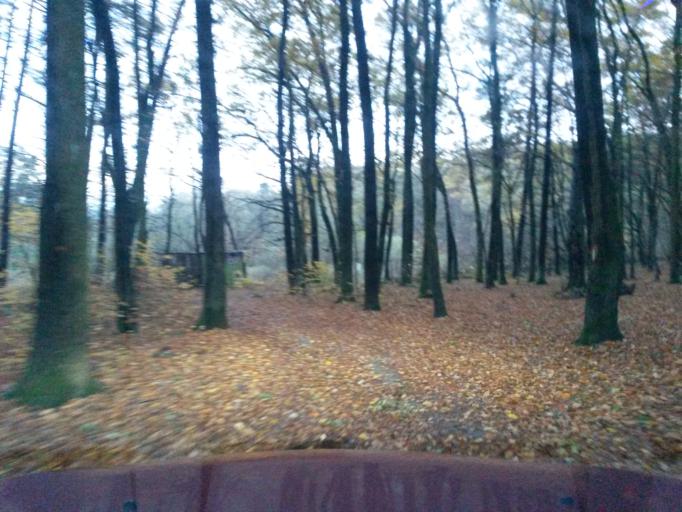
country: SK
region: Kosicky
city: Kosice
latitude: 48.7956
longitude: 21.2859
